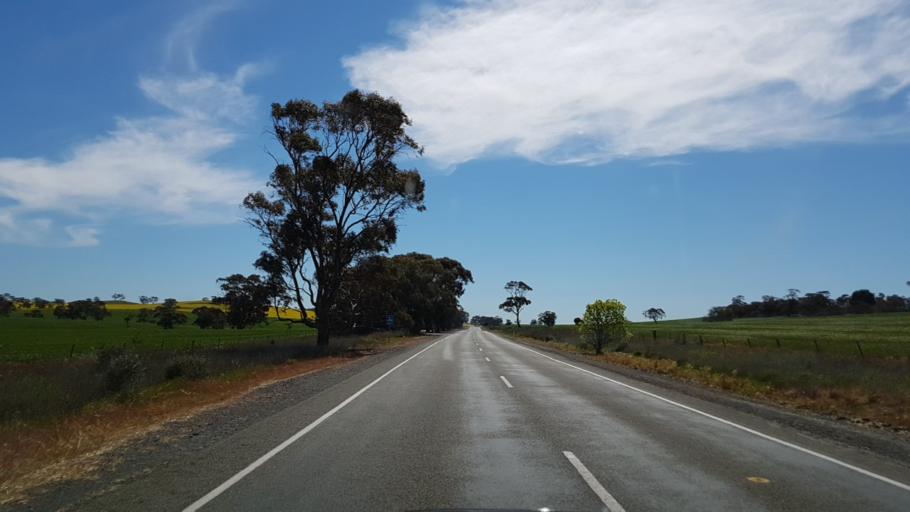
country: AU
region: South Australia
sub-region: Clare and Gilbert Valleys
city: Clare
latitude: -34.0496
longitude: 138.7974
